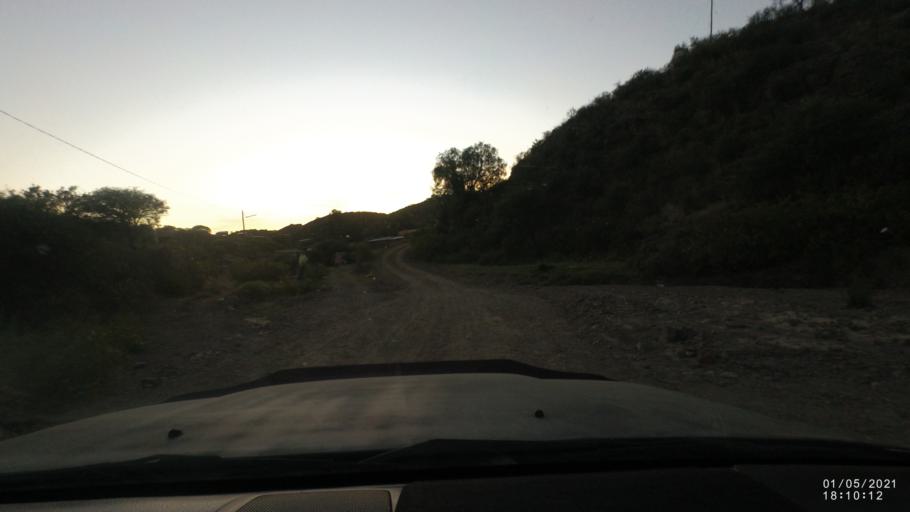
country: BO
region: Cochabamba
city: Capinota
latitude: -17.6852
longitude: -66.1958
